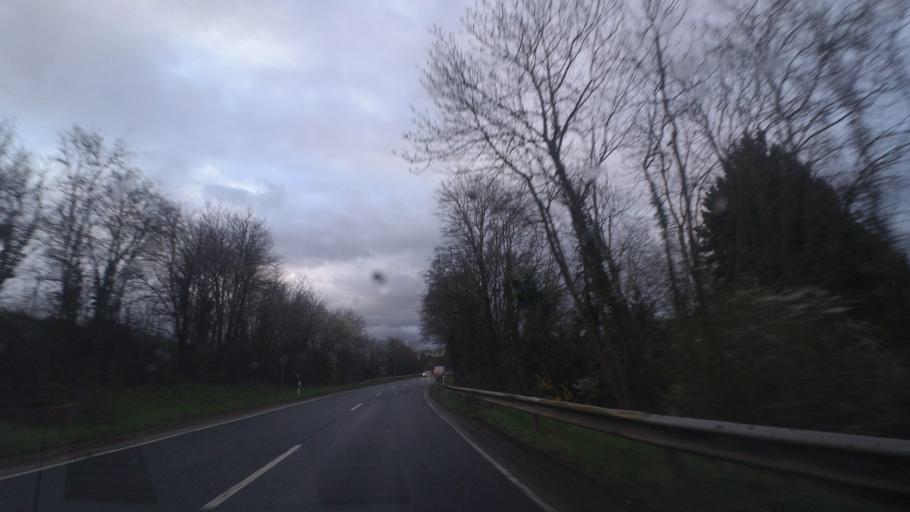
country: DE
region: Rheinland-Pfalz
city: Westhofen
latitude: 49.7024
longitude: 8.2383
